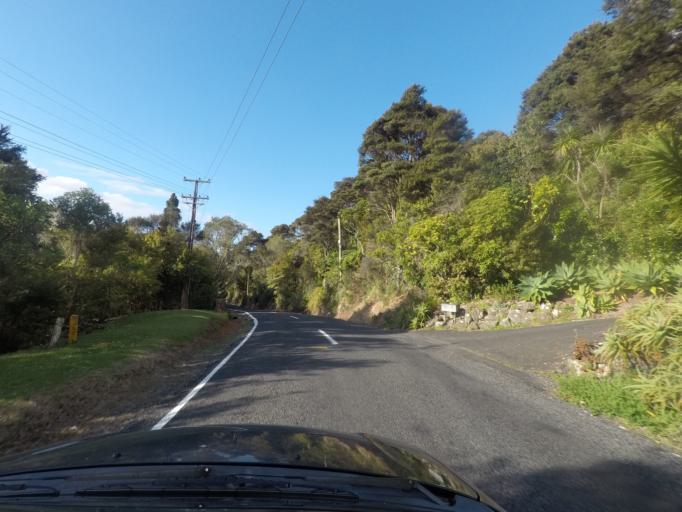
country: NZ
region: Auckland
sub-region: Auckland
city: Titirangi
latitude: -36.9392
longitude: 174.6225
